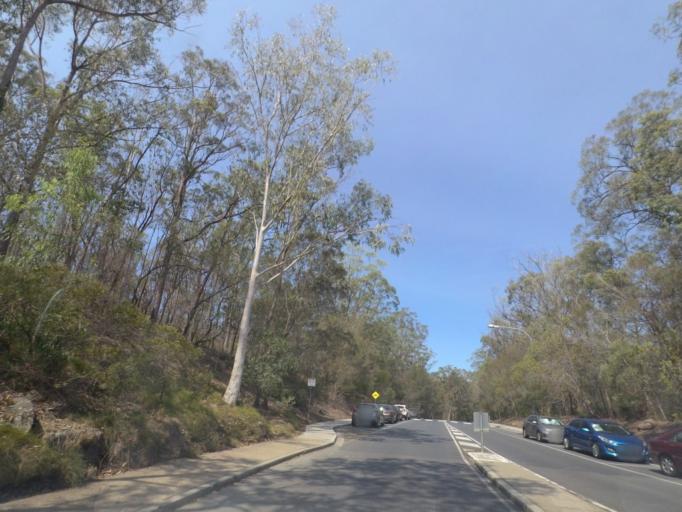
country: AU
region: Queensland
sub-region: Brisbane
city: Nathan
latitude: -27.5506
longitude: 153.0579
